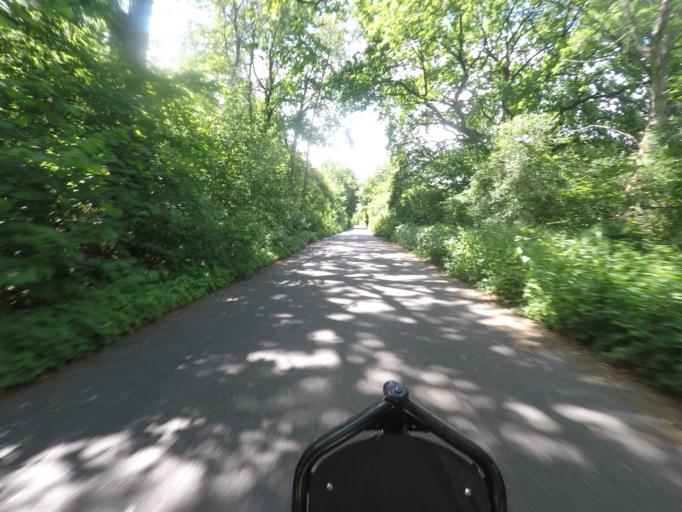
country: DE
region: Schleswig-Holstein
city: Stapelfeld
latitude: 53.6272
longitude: 10.1896
